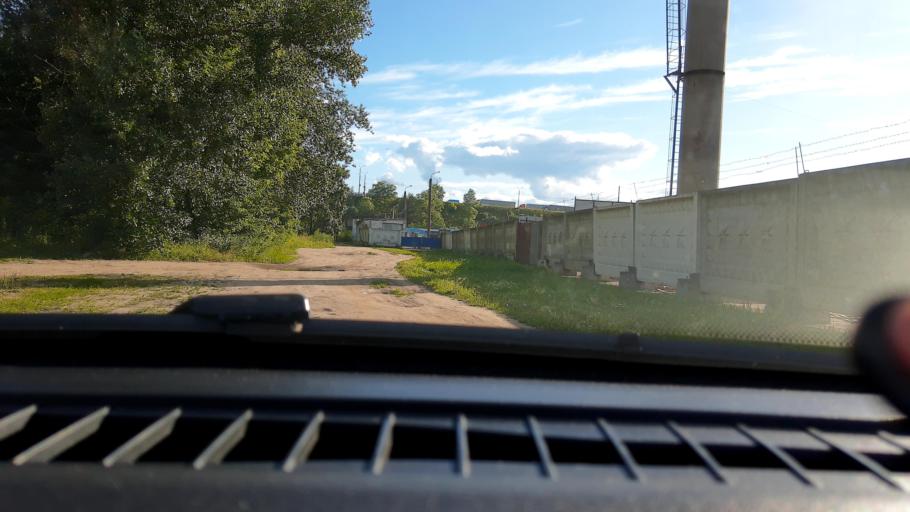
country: RU
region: Nizjnij Novgorod
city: Nizhniy Novgorod
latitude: 56.2556
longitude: 43.9442
